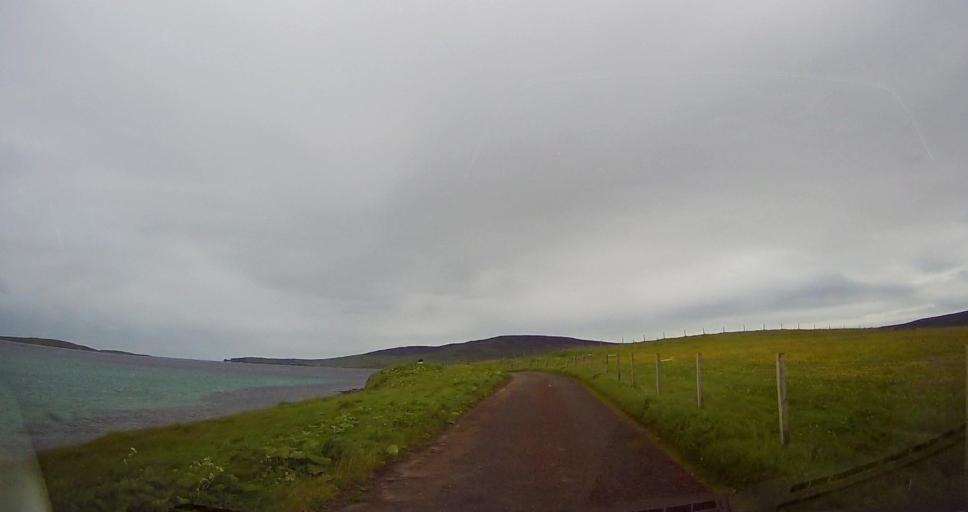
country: GB
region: Scotland
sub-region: Orkney Islands
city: Orkney
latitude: 59.1207
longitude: -3.0853
